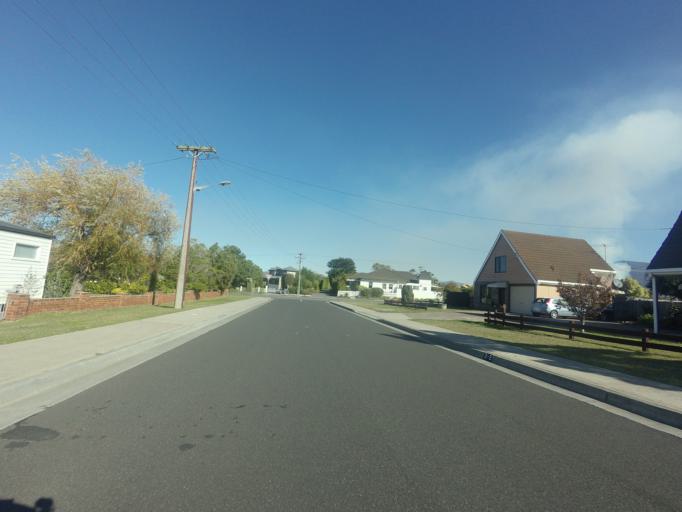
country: AU
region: Tasmania
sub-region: Clarence
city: Lindisfarne
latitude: -42.8490
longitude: 147.3466
